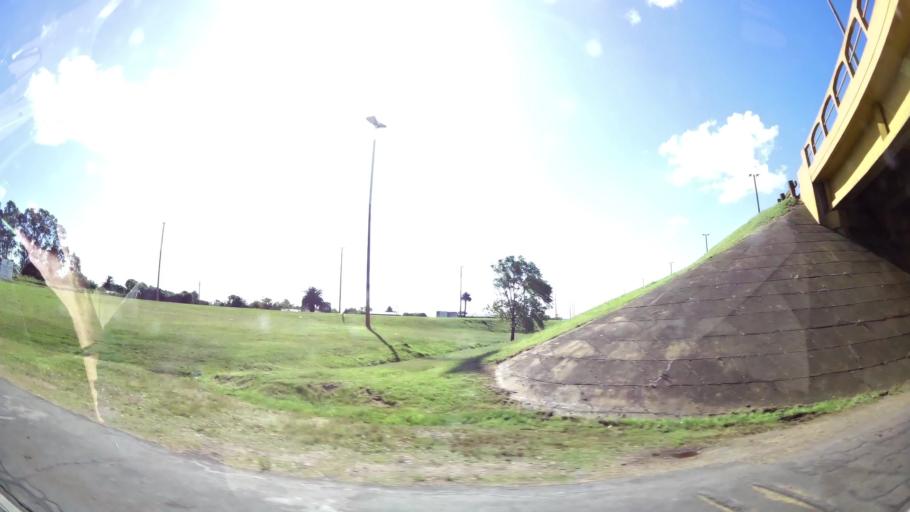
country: UY
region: Montevideo
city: Montevideo
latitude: -34.8574
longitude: -56.2567
